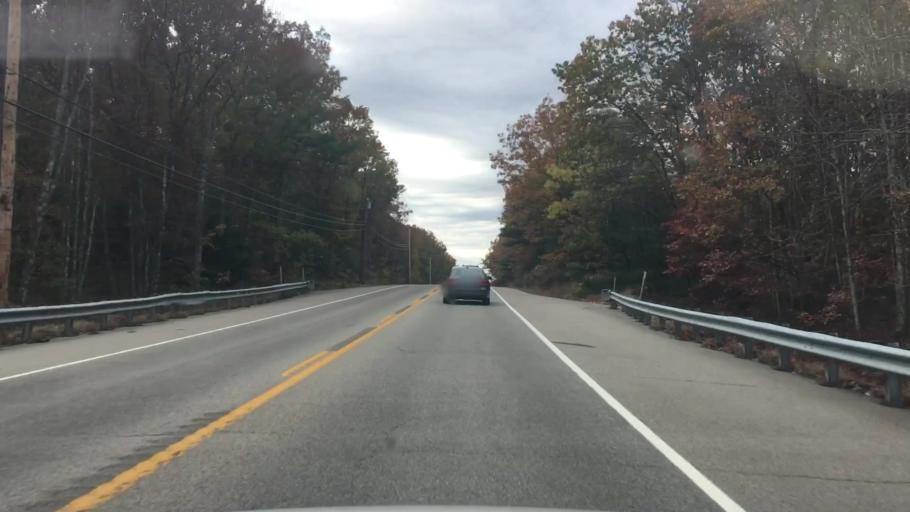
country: US
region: Maine
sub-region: York County
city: Alfred
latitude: 43.4767
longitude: -70.6490
